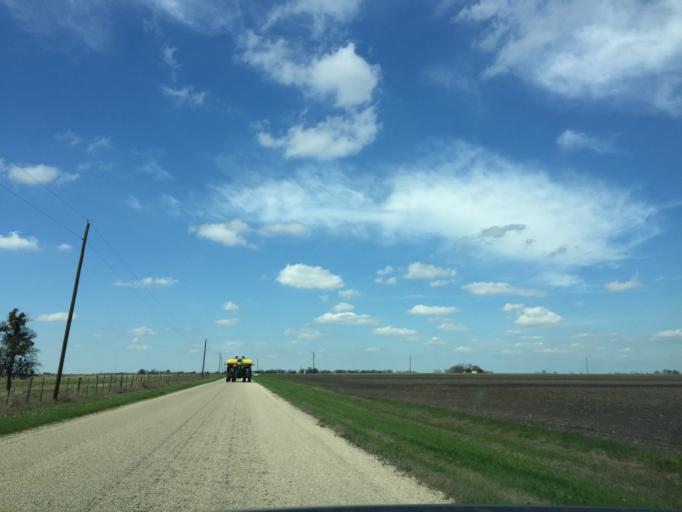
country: US
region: Texas
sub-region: Milam County
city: Thorndale
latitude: 30.5461
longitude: -97.2721
